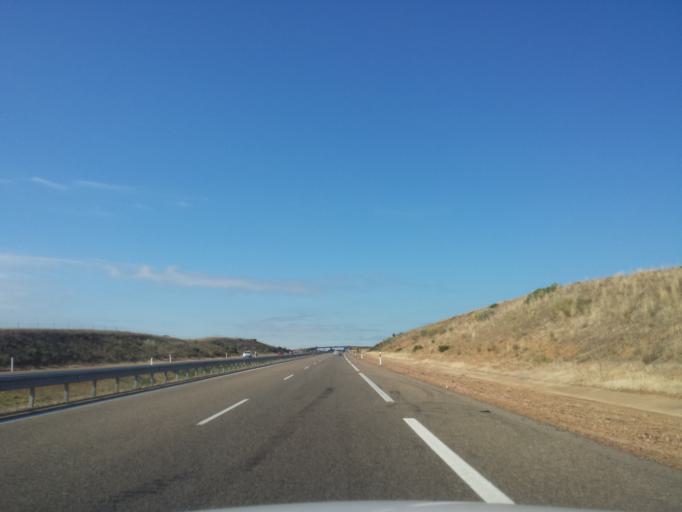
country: ES
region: Castille and Leon
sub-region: Provincia de Leon
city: Villamanan
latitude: 42.3499
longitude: -5.6017
